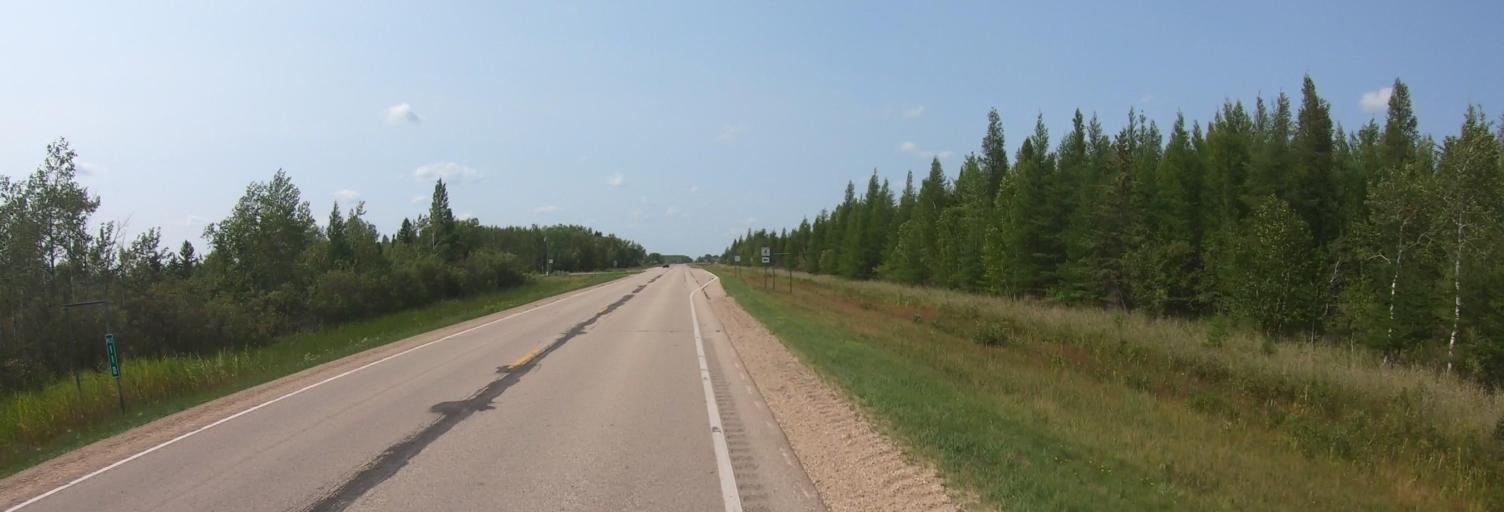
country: US
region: Minnesota
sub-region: Lake of the Woods County
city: Baudette
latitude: 48.7393
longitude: -94.8352
